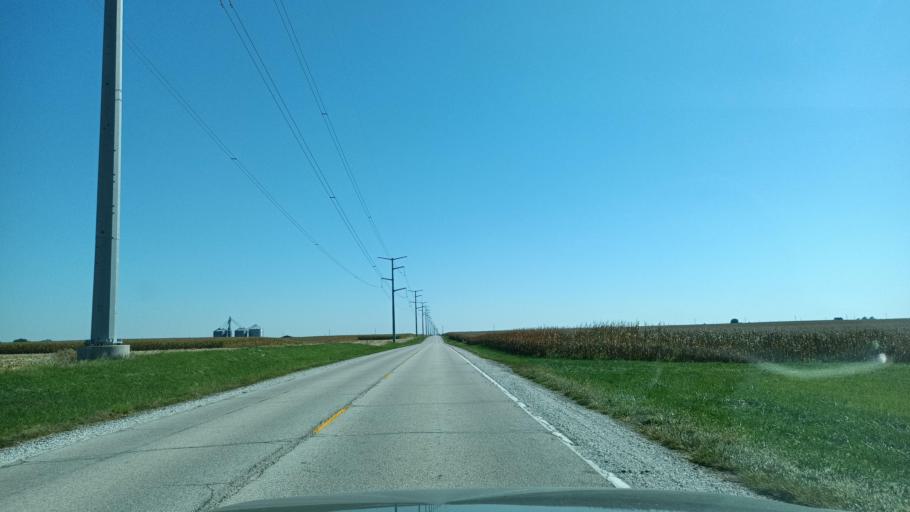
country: US
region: Illinois
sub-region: Peoria County
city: Elmwood
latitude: 40.9023
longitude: -90.0291
